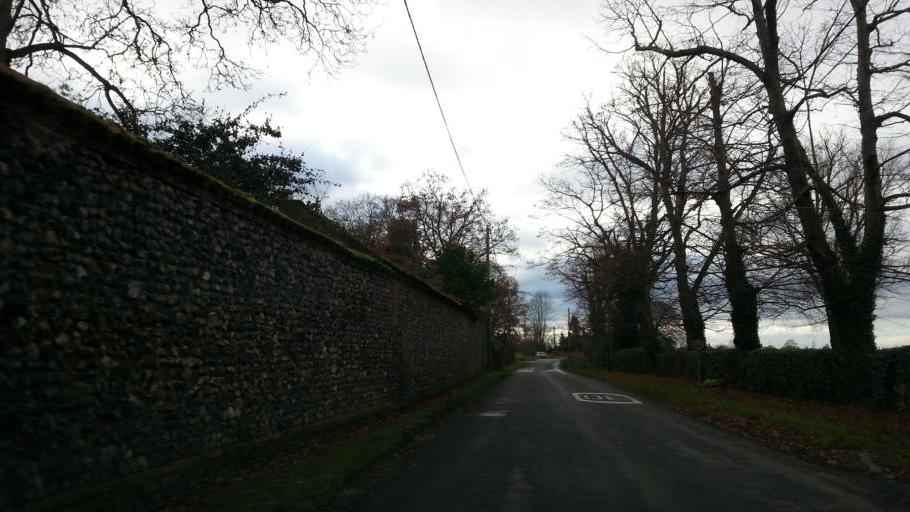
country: GB
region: England
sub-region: Suffolk
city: Ixworth
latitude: 52.3514
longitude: 0.8853
